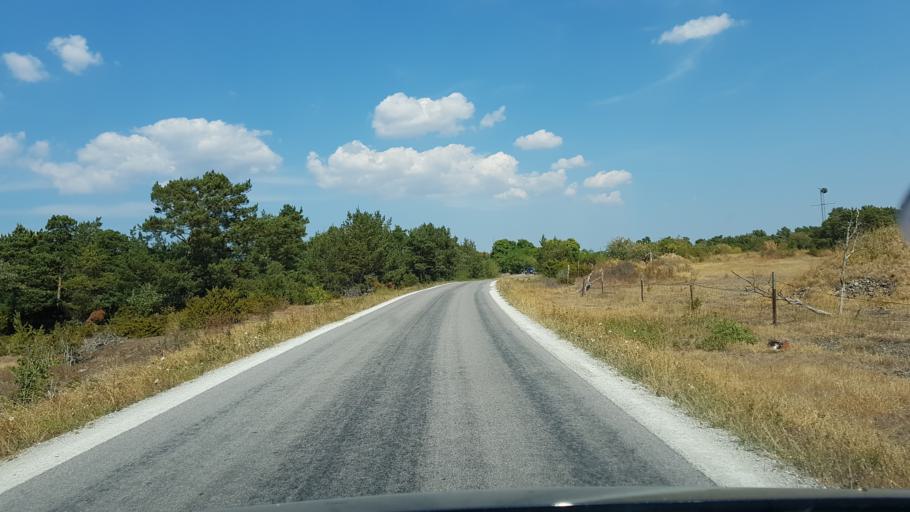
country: SE
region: Gotland
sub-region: Gotland
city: Visby
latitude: 57.6523
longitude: 18.3550
